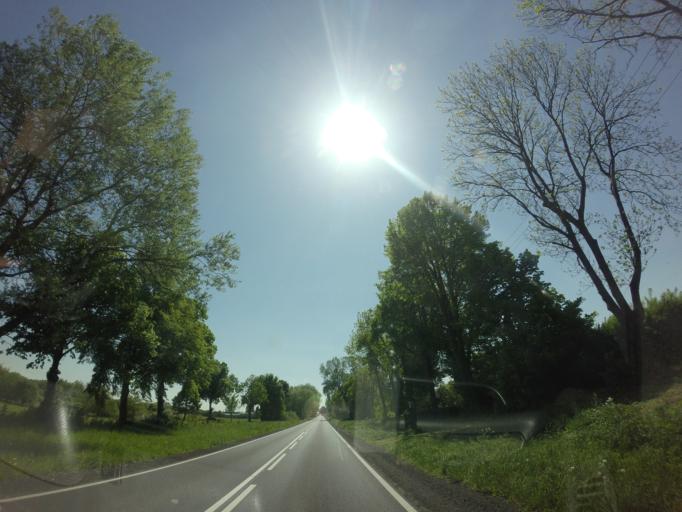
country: PL
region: West Pomeranian Voivodeship
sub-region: Powiat pyrzycki
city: Lipiany
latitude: 52.9981
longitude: 14.9799
